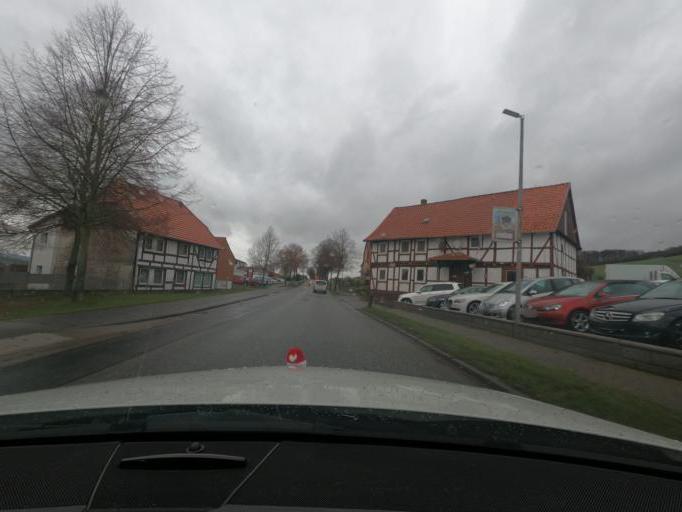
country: DE
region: Lower Saxony
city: Northeim
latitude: 51.7660
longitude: 9.9577
